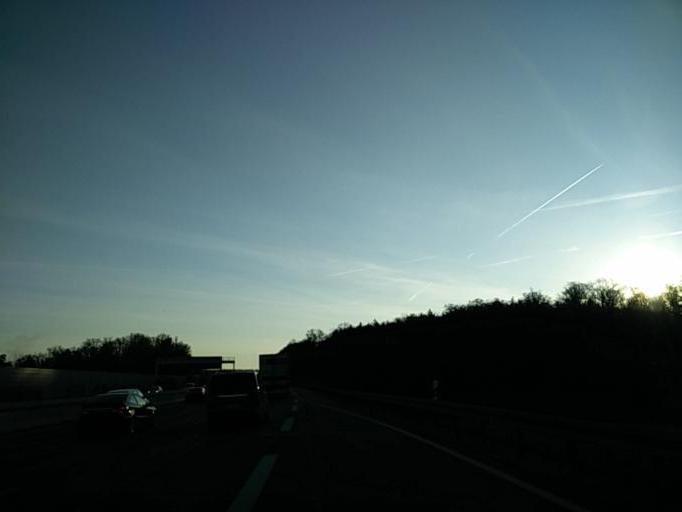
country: DE
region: Baden-Wuerttemberg
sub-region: Regierungsbezirk Stuttgart
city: Ehningen
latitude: 48.6489
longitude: 8.9471
